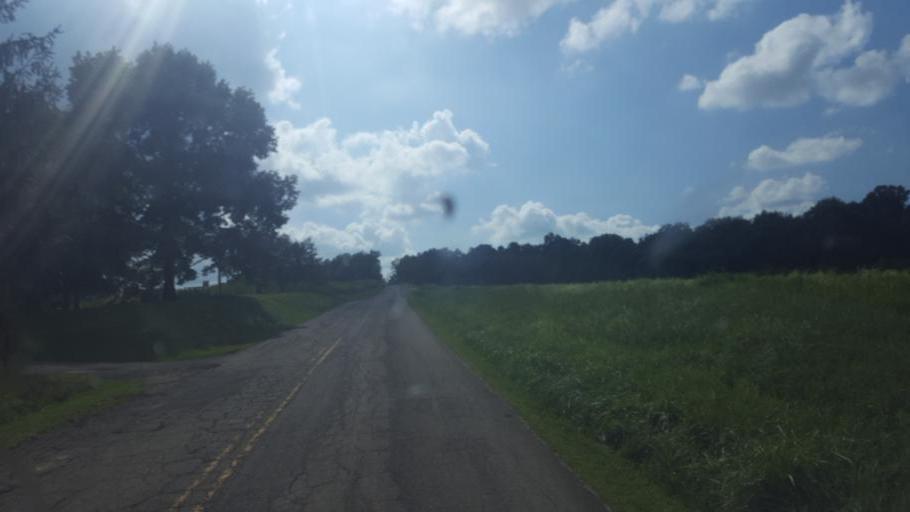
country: US
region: Ohio
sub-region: Knox County
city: Oak Hill
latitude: 40.4102
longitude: -82.2455
